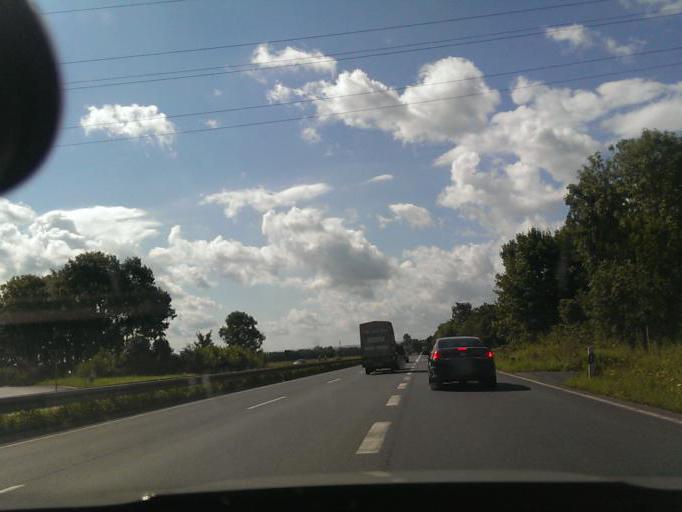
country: DE
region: Lower Saxony
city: Laatzen
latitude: 52.2995
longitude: 9.8296
